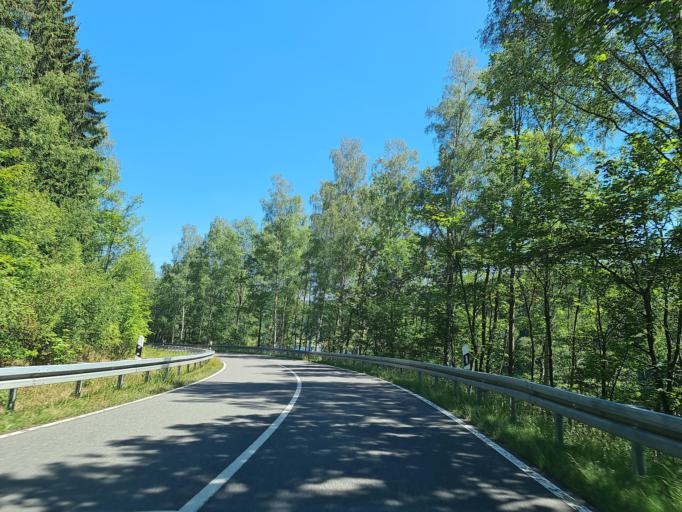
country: DE
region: Saxony
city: Rechenberg-Bienenmuhle
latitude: 50.7064
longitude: 13.5292
